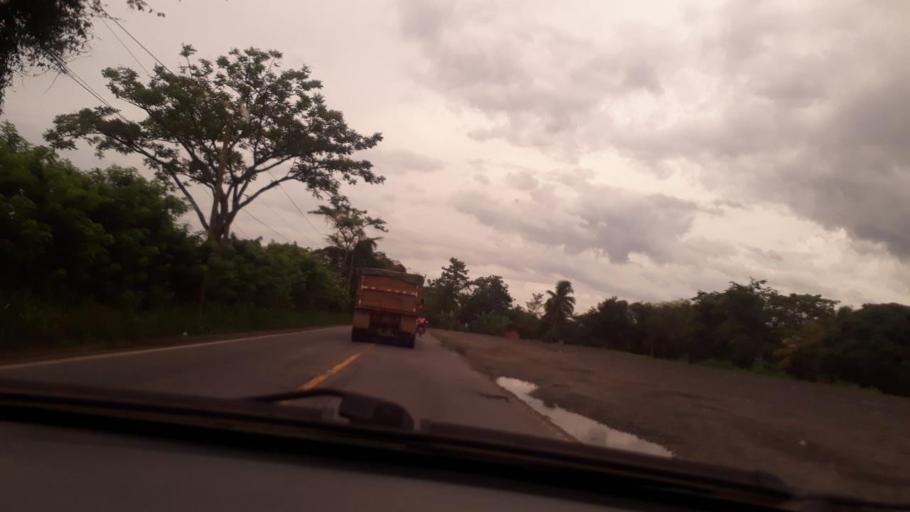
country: GT
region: Izabal
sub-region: Municipio de Los Amates
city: Los Amates
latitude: 15.3046
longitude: -89.0594
